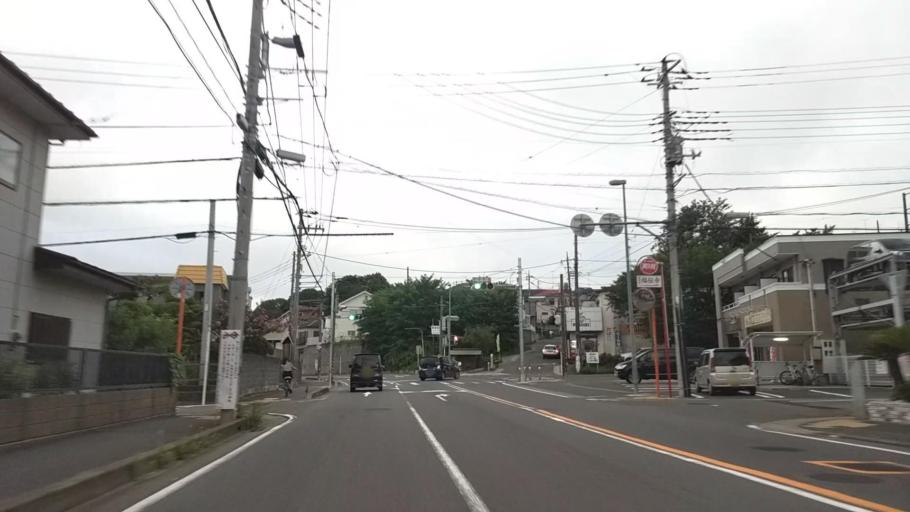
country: JP
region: Kanagawa
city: Atsugi
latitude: 35.4564
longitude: 139.3482
